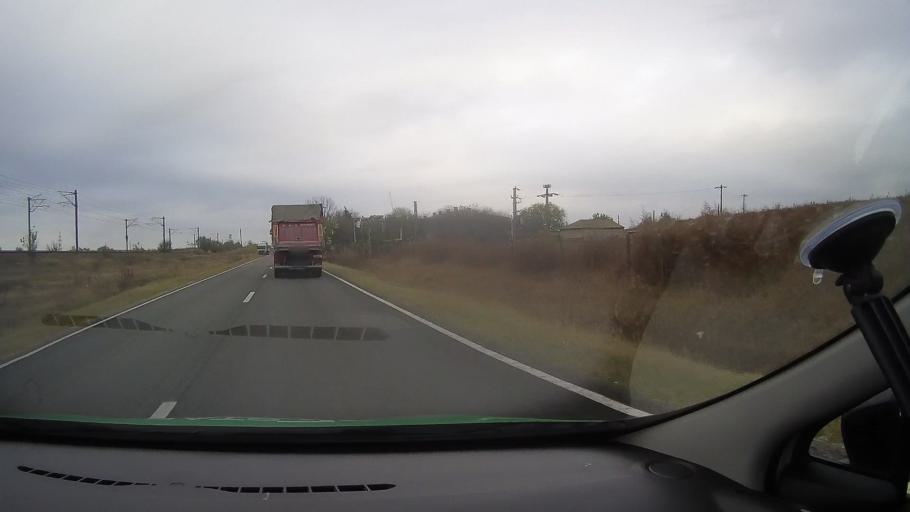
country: RO
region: Constanta
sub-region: Comuna Poarta Alba
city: Poarta Alba
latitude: 44.2260
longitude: 28.3827
